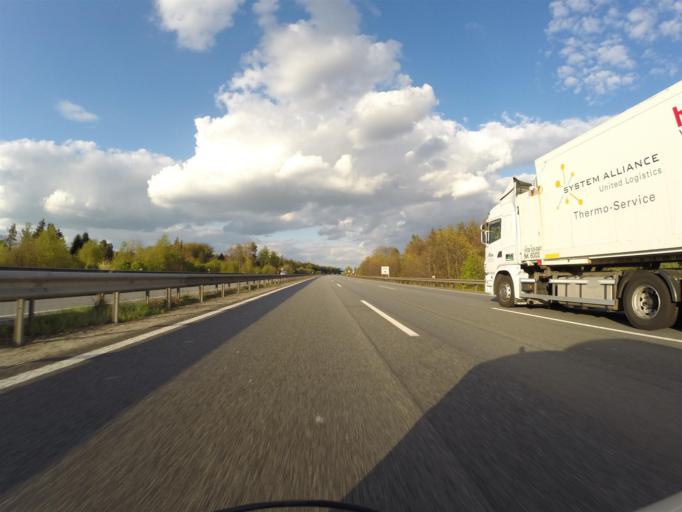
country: DE
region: Rheinland-Pfalz
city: Rodenbach
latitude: 49.4378
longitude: 7.6415
